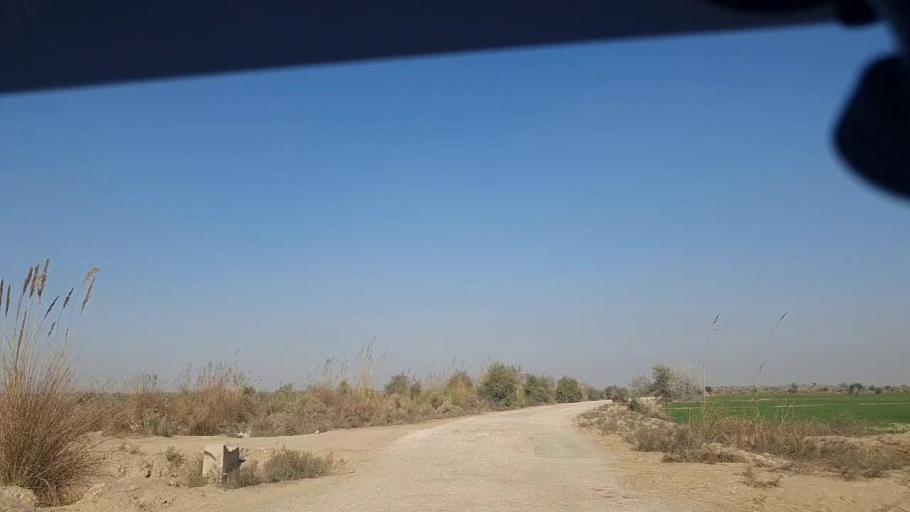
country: PK
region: Sindh
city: Khanpur
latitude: 27.5659
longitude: 69.3392
